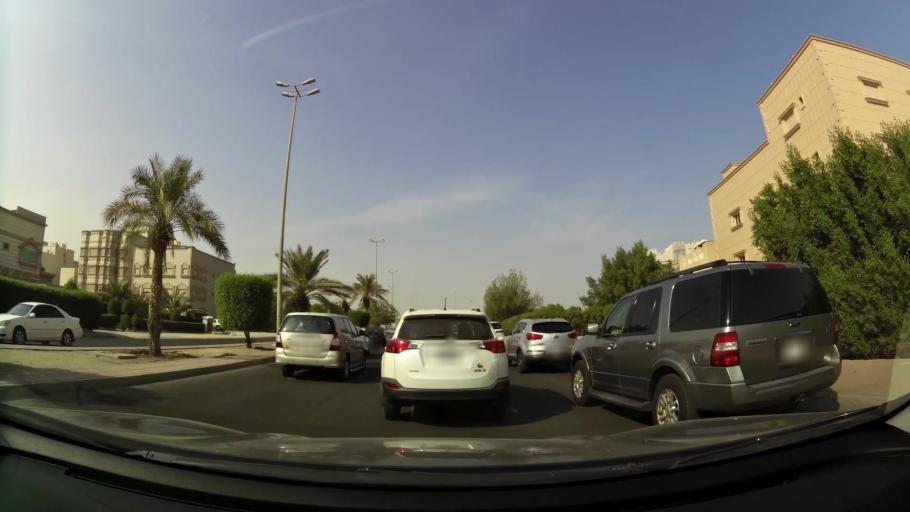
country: KW
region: Mubarak al Kabir
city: Mubarak al Kabir
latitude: 29.1732
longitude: 48.0849
